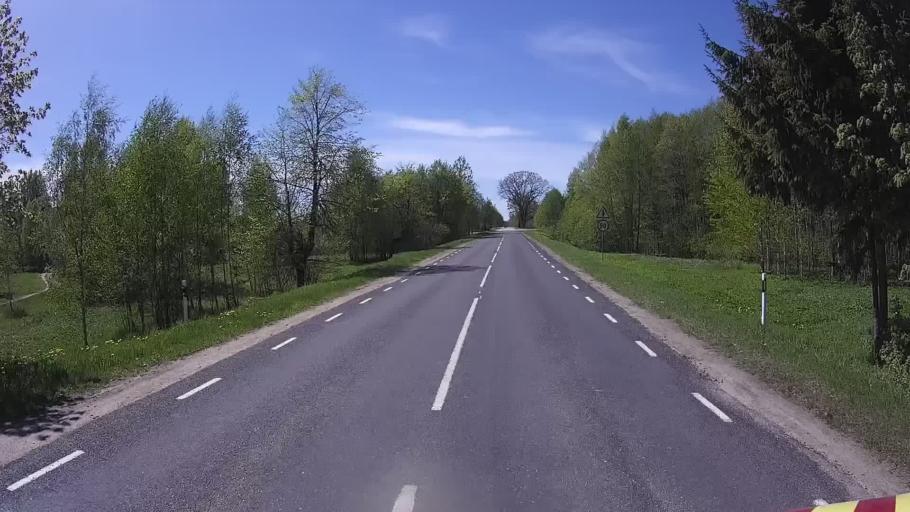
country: EE
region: Polvamaa
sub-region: Raepina vald
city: Rapina
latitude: 57.9925
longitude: 27.3324
